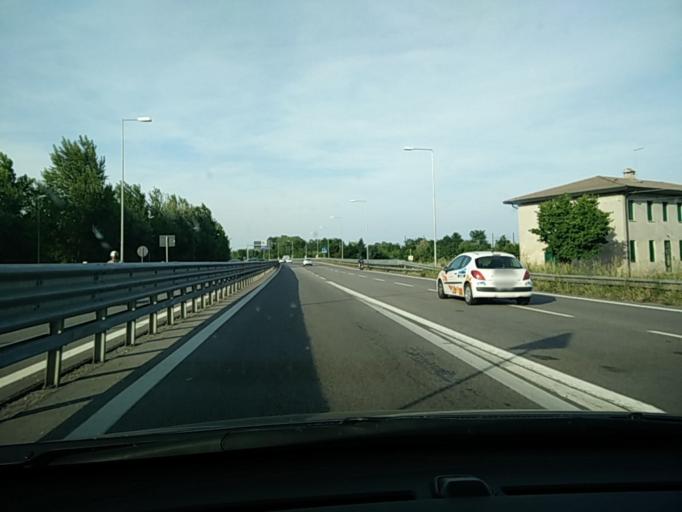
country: IT
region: Veneto
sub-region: Provincia di Padova
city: Mandriola-Sant'Agostino
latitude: 45.3839
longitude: 11.8314
